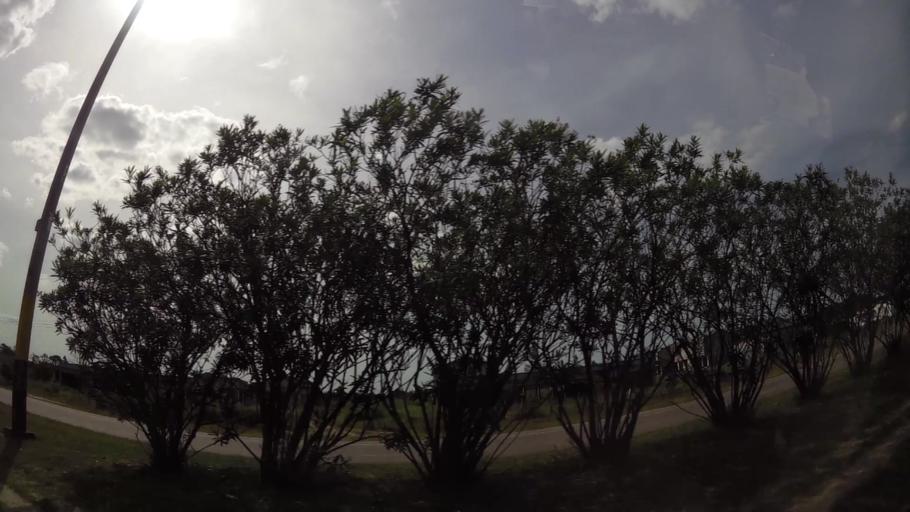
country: UY
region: Canelones
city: Pando
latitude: -34.8058
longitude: -55.9291
